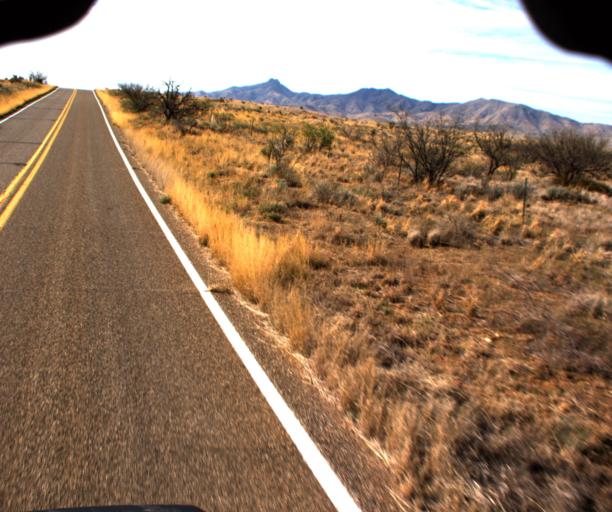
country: US
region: Arizona
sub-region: Cochise County
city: Willcox
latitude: 32.0998
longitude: -109.5410
